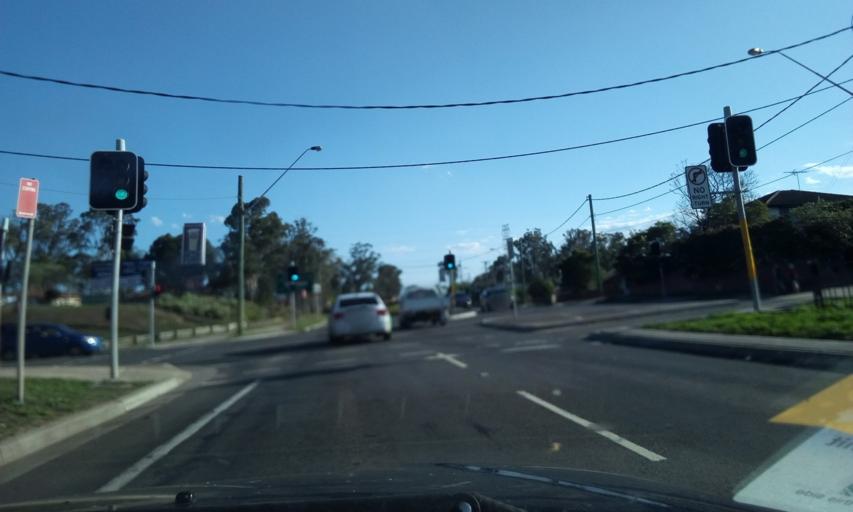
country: AU
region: New South Wales
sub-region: Penrith Municipality
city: Cambridge Park
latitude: -33.7407
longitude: 150.7165
